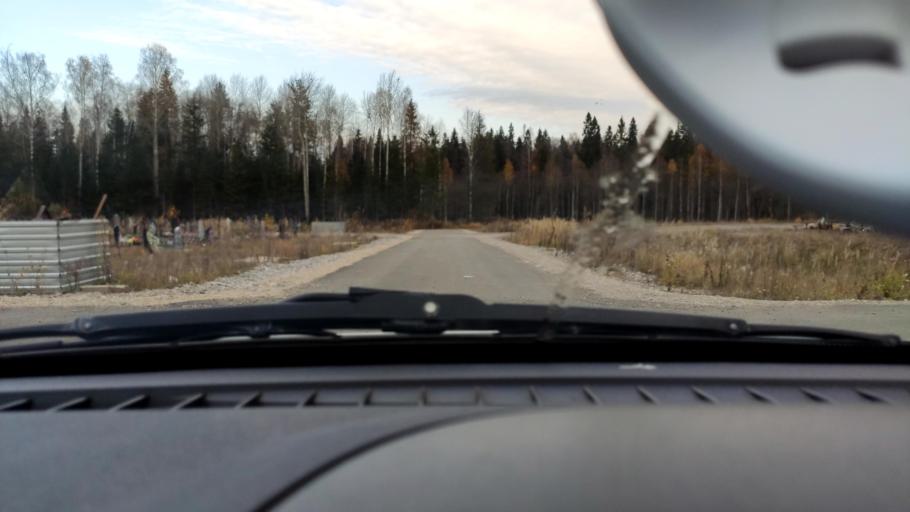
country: RU
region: Perm
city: Kondratovo
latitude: 58.0709
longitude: 56.1347
